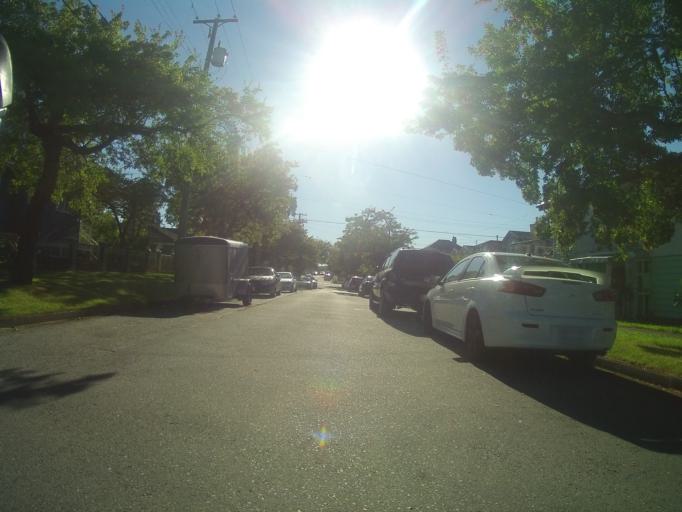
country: CA
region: British Columbia
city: Vancouver
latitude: 49.2430
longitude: -123.0710
